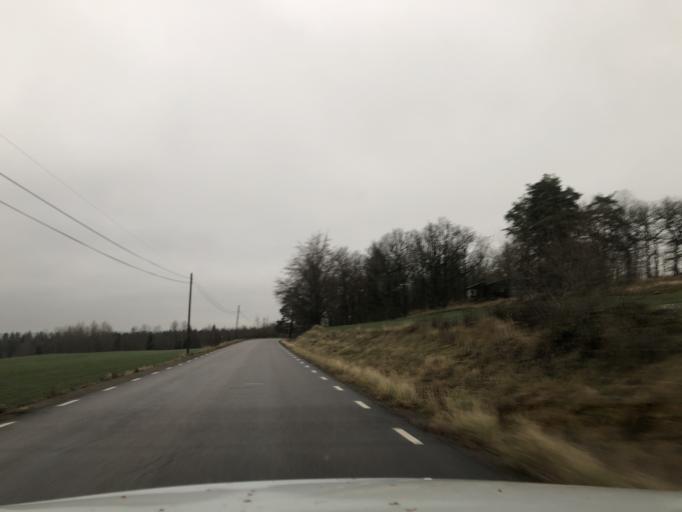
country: SE
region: Vaestra Goetaland
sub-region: Ulricehamns Kommun
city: Ulricehamn
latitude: 57.8506
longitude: 13.3884
